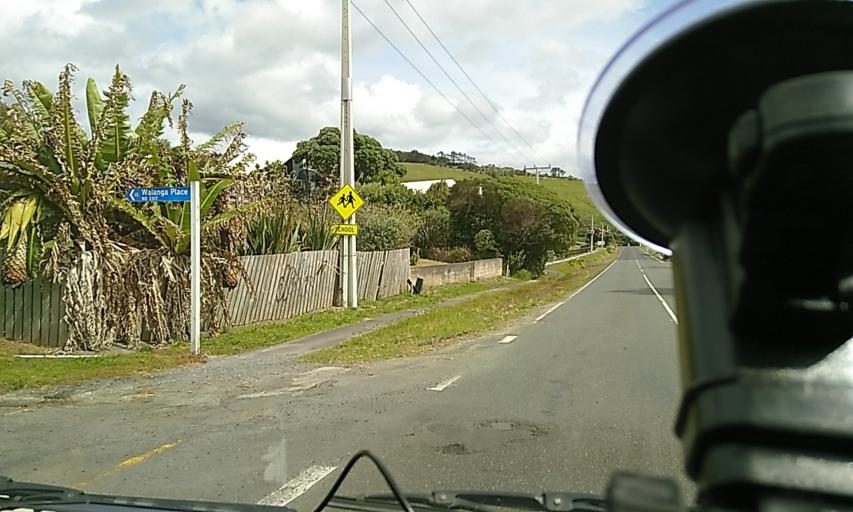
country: NZ
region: Northland
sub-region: Far North District
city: Ahipara
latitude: -35.5274
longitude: 173.3898
